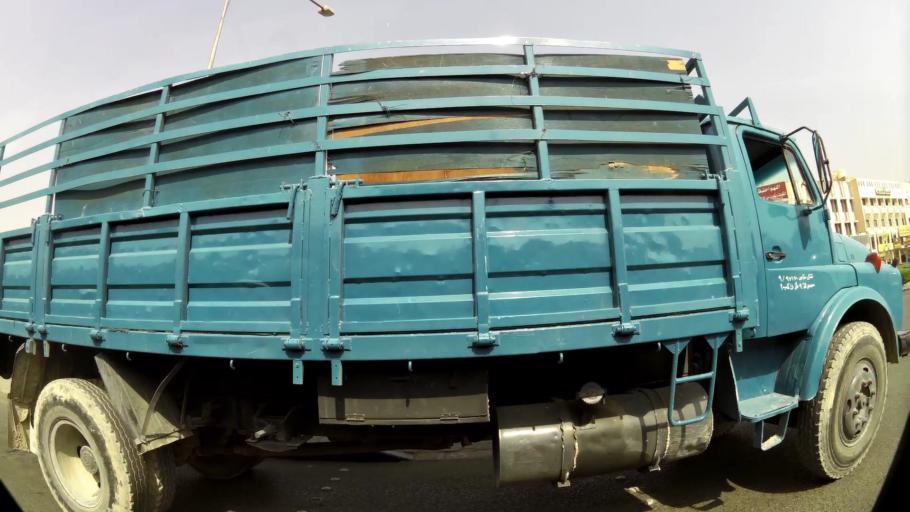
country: KW
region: Al Farwaniyah
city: Al Farwaniyah
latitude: 29.2594
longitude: 47.9396
